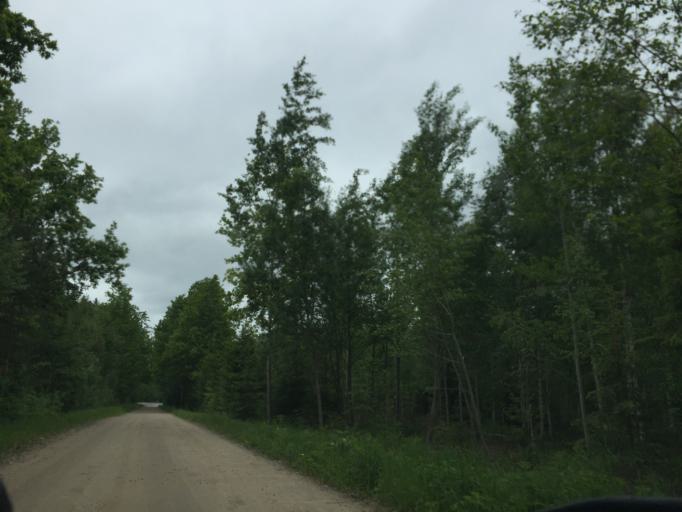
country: LV
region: Valmieras Rajons
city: Valmiera
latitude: 57.5802
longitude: 25.5077
